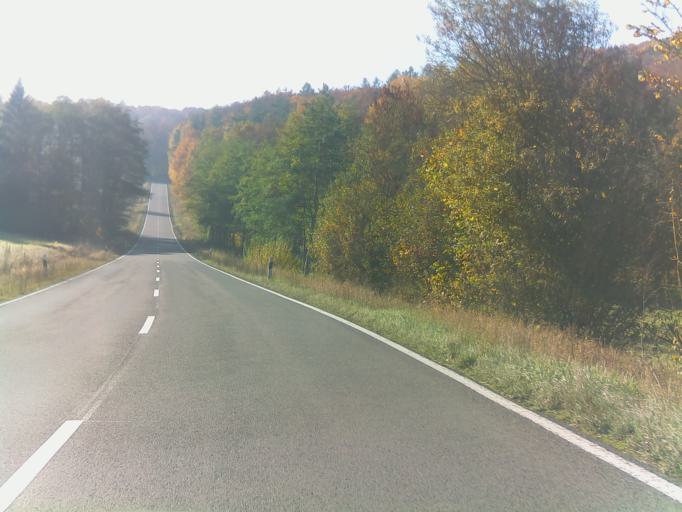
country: DE
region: Bavaria
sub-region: Regierungsbezirk Unterfranken
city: Sand
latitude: 49.9390
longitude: 10.5971
